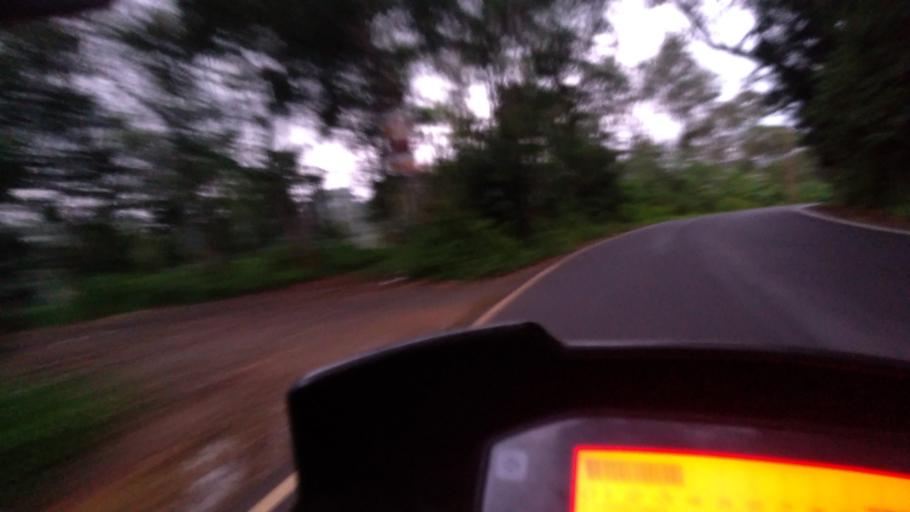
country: IN
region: Kerala
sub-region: Idukki
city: Munnar
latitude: 9.9559
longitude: 77.0824
